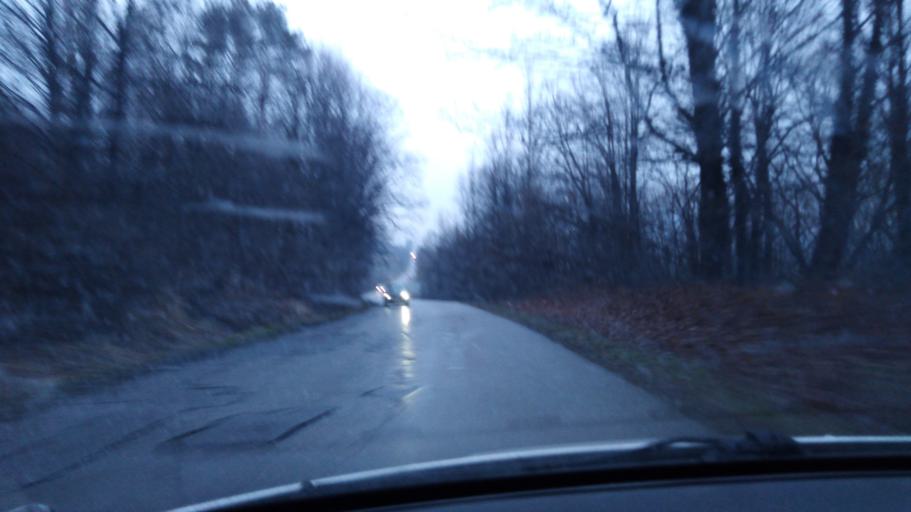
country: PL
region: Silesian Voivodeship
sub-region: Powiat zywiecki
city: Radziechowy
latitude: 49.6338
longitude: 19.1538
